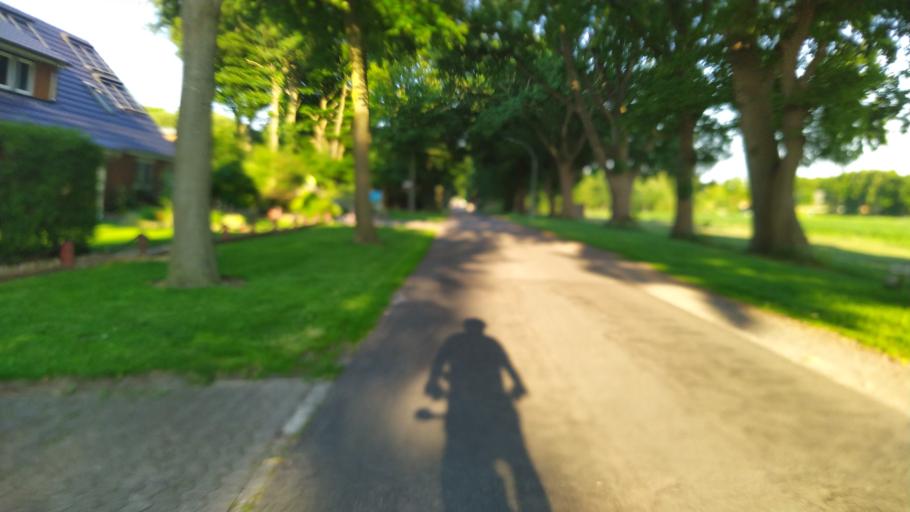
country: DE
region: Lower Saxony
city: Alfstedt
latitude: 53.5497
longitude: 9.0625
